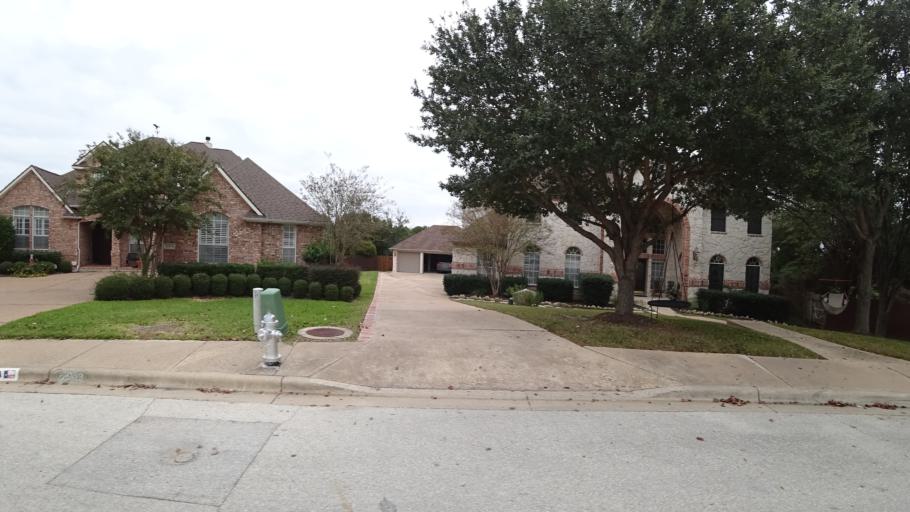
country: US
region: Texas
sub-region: Travis County
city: Bee Cave
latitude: 30.3158
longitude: -97.9286
